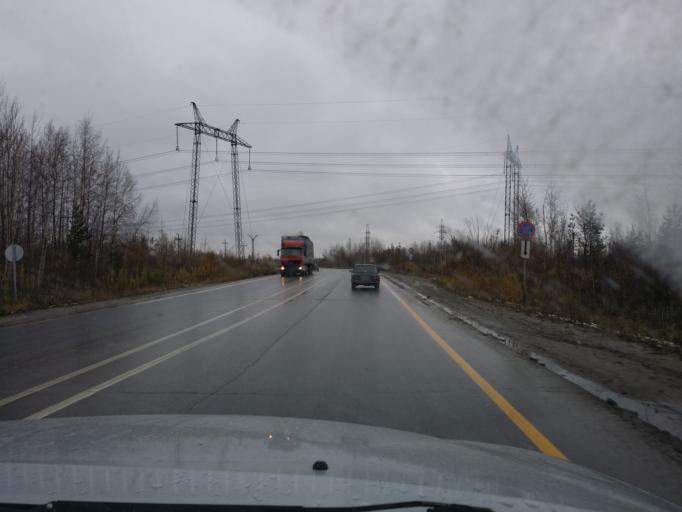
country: RU
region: Khanty-Mansiyskiy Avtonomnyy Okrug
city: Megion
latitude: 61.0808
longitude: 76.1175
